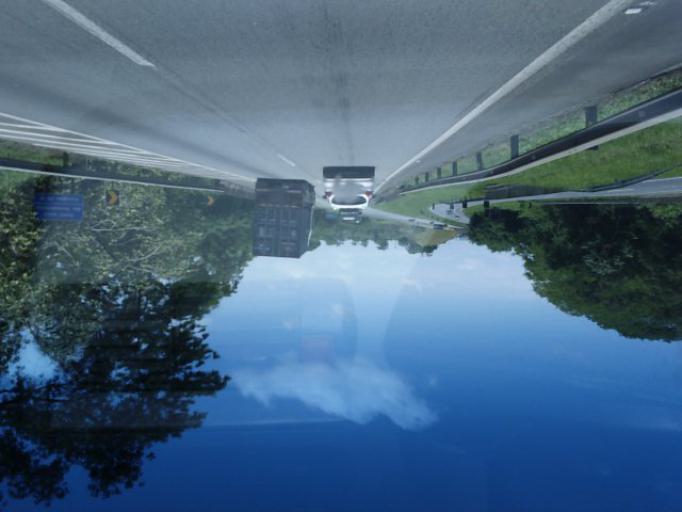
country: BR
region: Sao Paulo
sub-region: Juquia
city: Juquia
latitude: -24.3298
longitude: -47.6174
